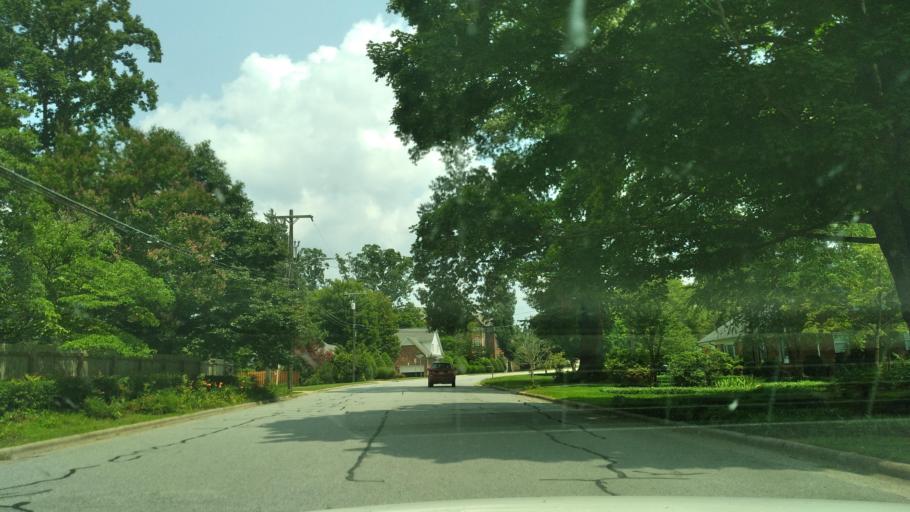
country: US
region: North Carolina
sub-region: Guilford County
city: Greensboro
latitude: 36.1206
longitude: -79.8501
